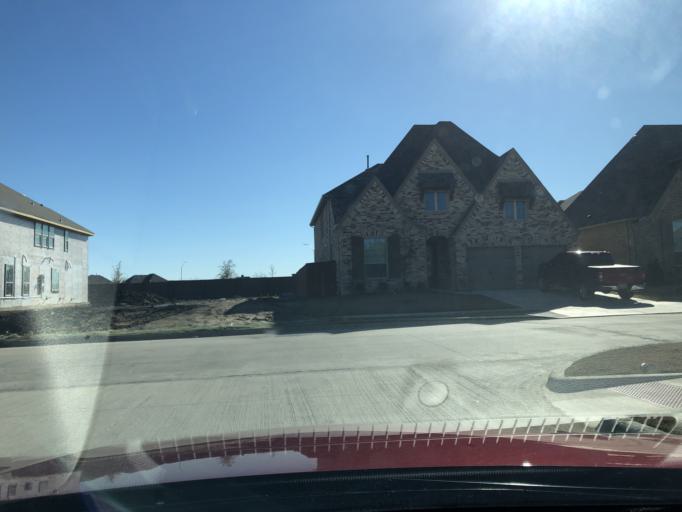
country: US
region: Texas
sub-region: Tarrant County
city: Haslet
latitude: 32.9466
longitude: -97.3959
